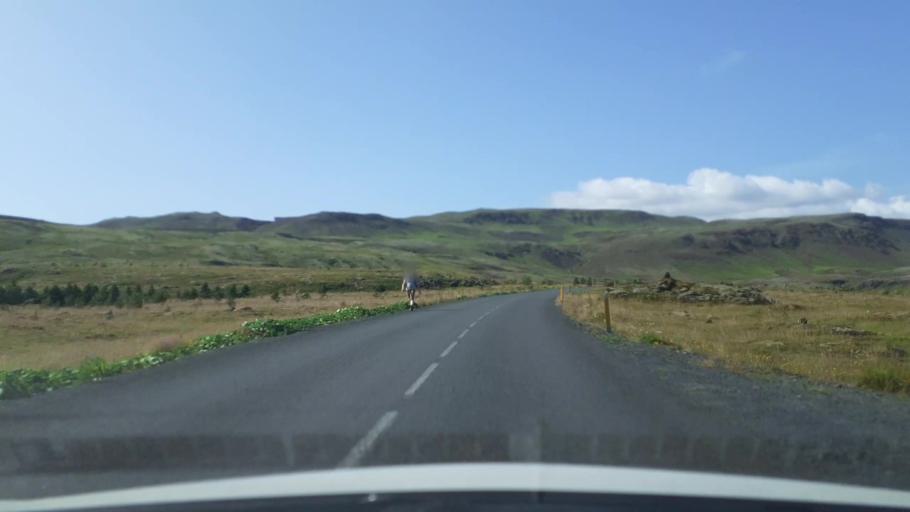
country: IS
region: South
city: Hveragerdi
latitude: 64.0135
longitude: -21.2060
